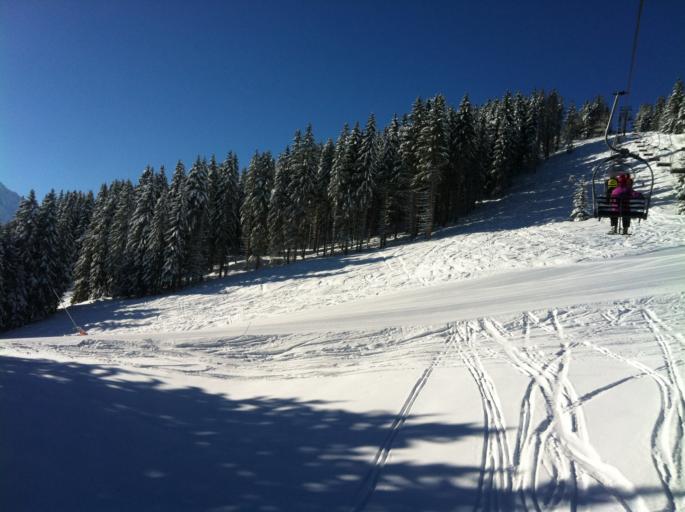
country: FR
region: Rhone-Alpes
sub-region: Departement de la Haute-Savoie
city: Saint-Gervais-les-Bains
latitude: 45.8551
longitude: 6.7092
